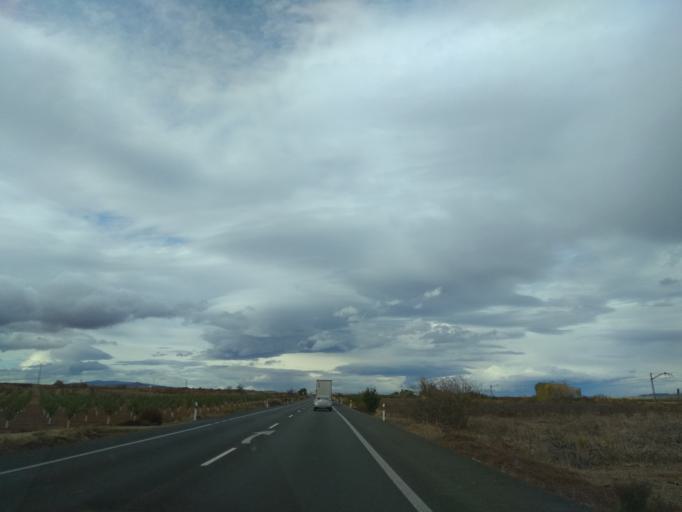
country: ES
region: La Rioja
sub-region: Provincia de La Rioja
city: Rincon de Soto
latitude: 42.2167
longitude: -1.8211
